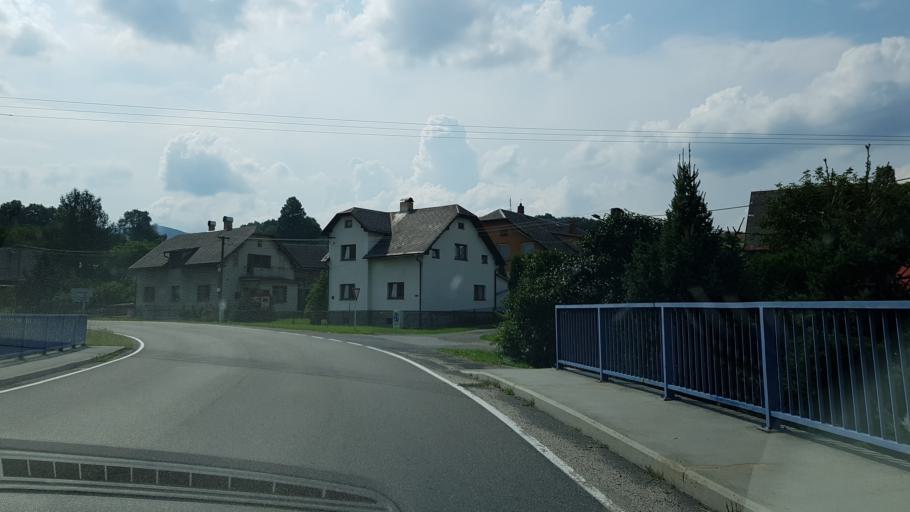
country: CZ
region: Olomoucky
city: Pisecna
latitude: 50.2719
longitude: 17.2798
